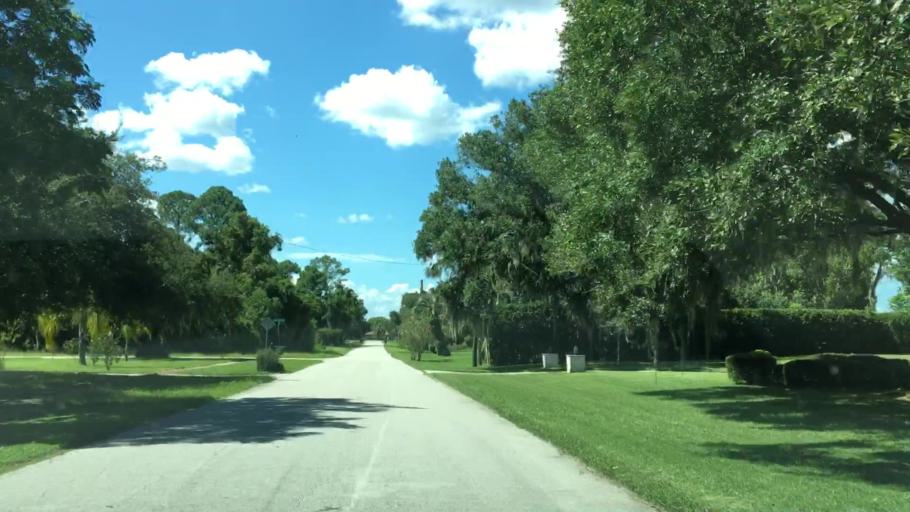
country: US
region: Florida
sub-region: Volusia County
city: Deltona
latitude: 28.8801
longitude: -81.2248
